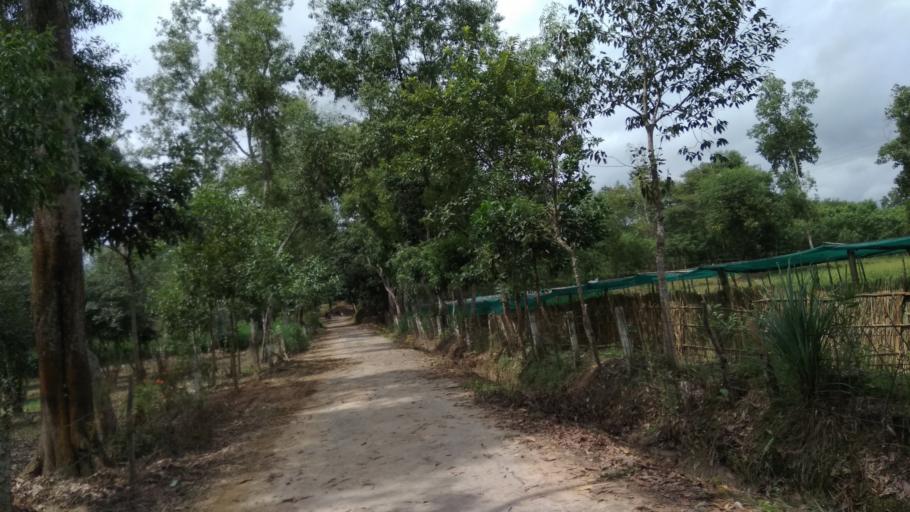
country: IN
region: Tripura
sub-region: Dhalai
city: Kamalpur
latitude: 24.2825
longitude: 91.8230
